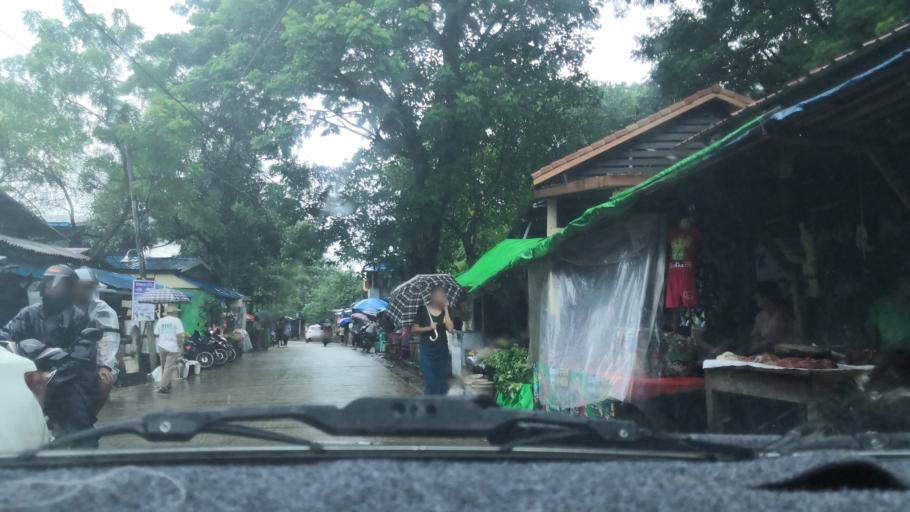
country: MM
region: Yangon
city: Yangon
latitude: 16.8776
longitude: 96.1494
